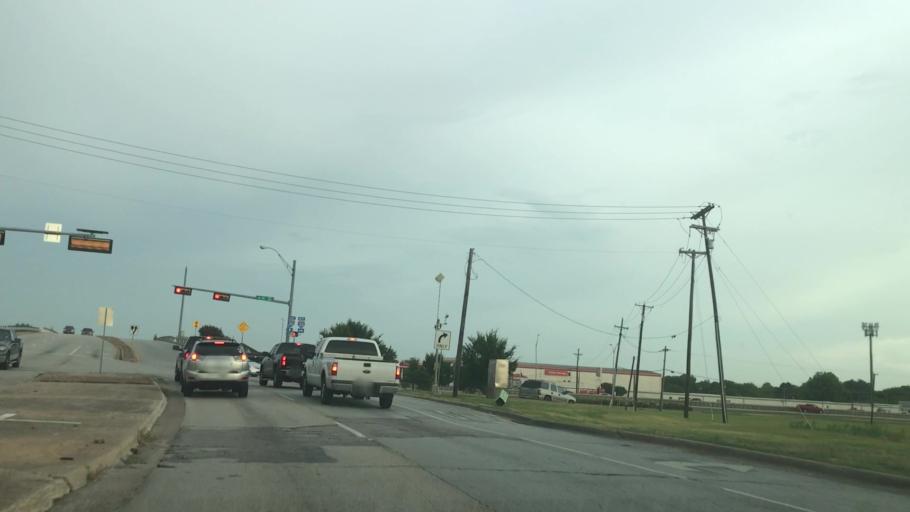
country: US
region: Texas
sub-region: Dallas County
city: Mesquite
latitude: 32.8113
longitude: -96.6564
